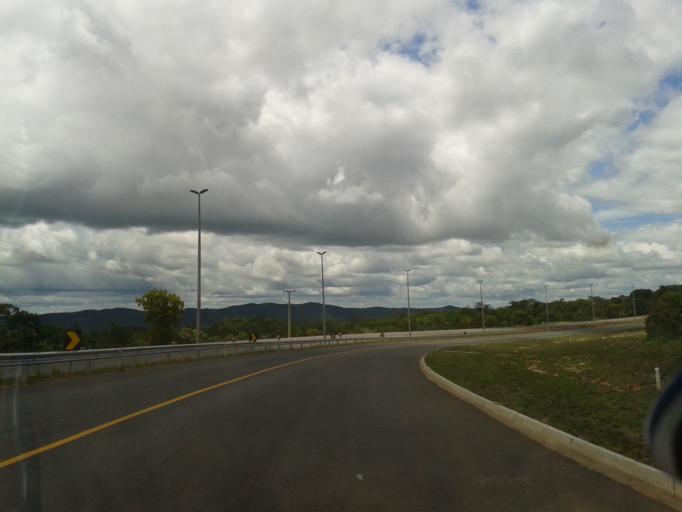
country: BR
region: Goias
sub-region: Goias
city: Goias
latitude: -15.9797
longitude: -50.0992
